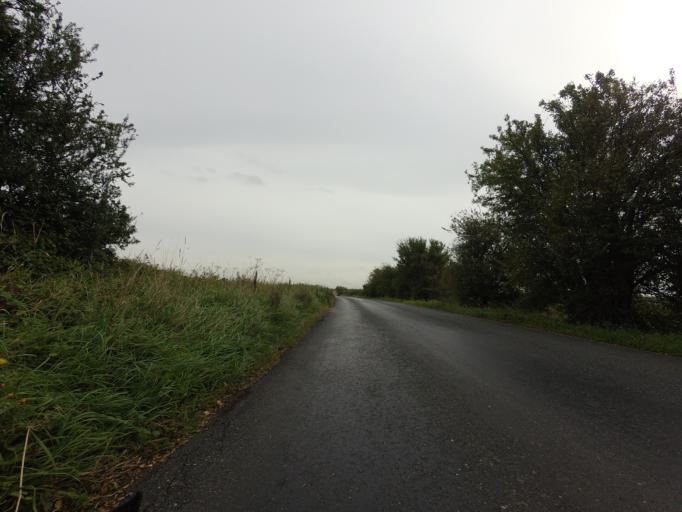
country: GB
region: England
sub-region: Hertfordshire
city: Reed
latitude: 51.9930
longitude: 0.0251
